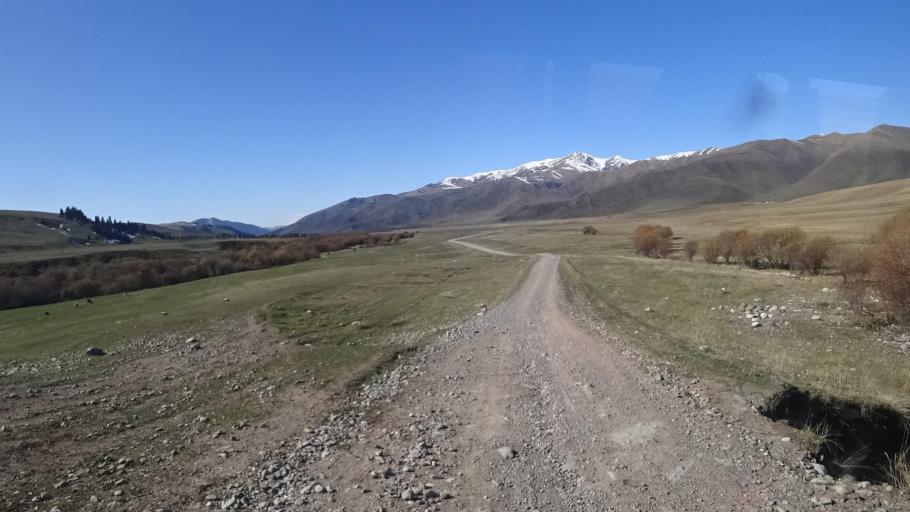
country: KZ
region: Almaty Oblysy
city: Kegen
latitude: 42.7364
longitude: 79.0156
